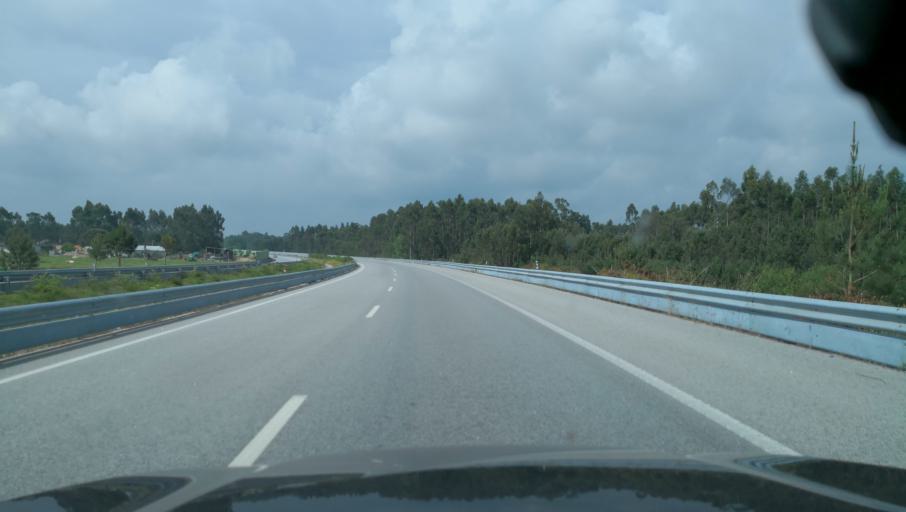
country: PT
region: Coimbra
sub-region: Montemor-O-Velho
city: Arazede
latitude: 40.3020
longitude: -8.7378
